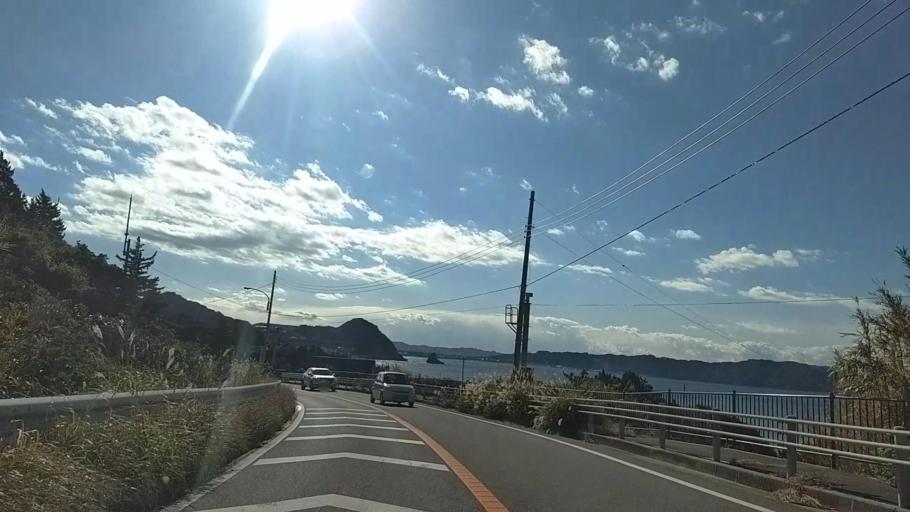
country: JP
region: Chiba
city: Tateyama
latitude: 35.0652
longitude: 139.8242
